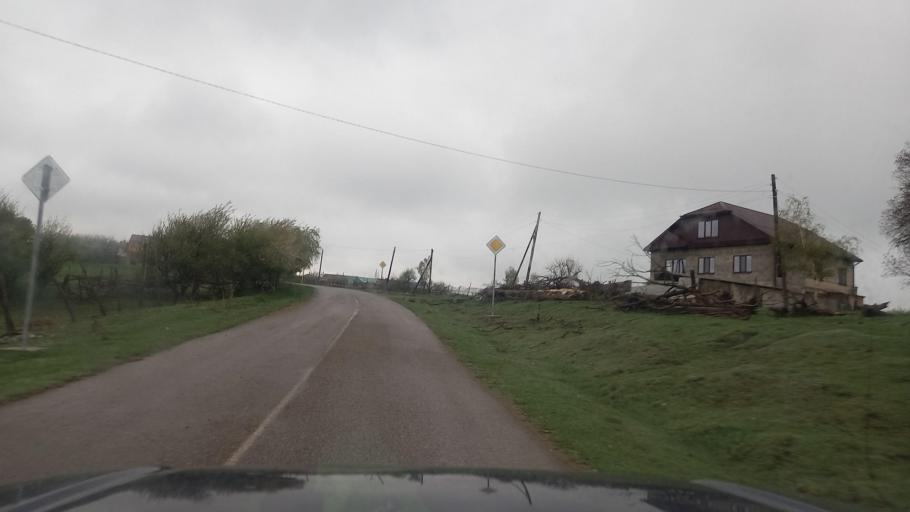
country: RU
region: Stavropol'skiy
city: Nezhinskiy
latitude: 43.8635
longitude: 42.6504
